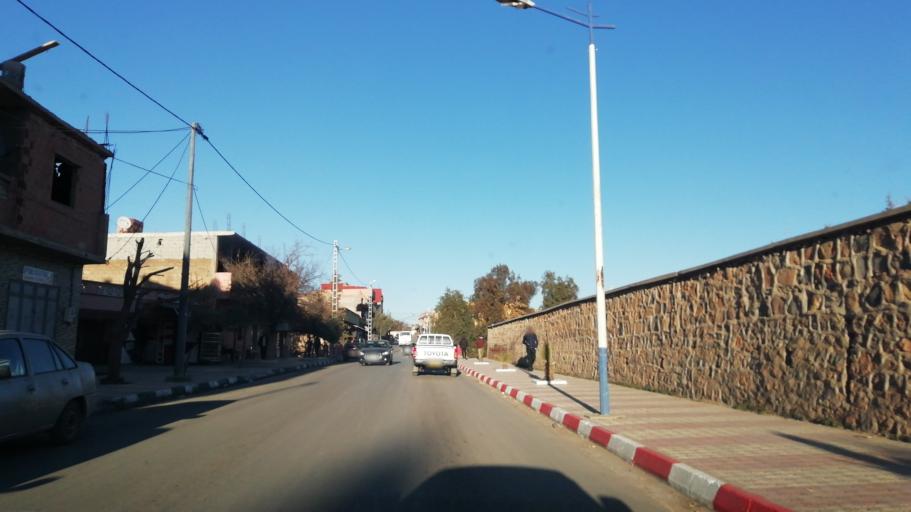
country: DZ
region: Tlemcen
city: Sebdou
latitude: 34.6451
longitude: -1.3247
